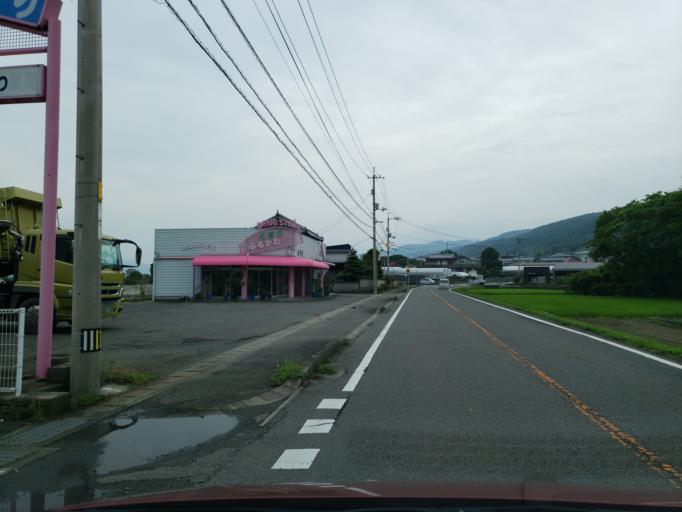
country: JP
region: Tokushima
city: Kamojimacho-jogejima
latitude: 34.1040
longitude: 134.2671
